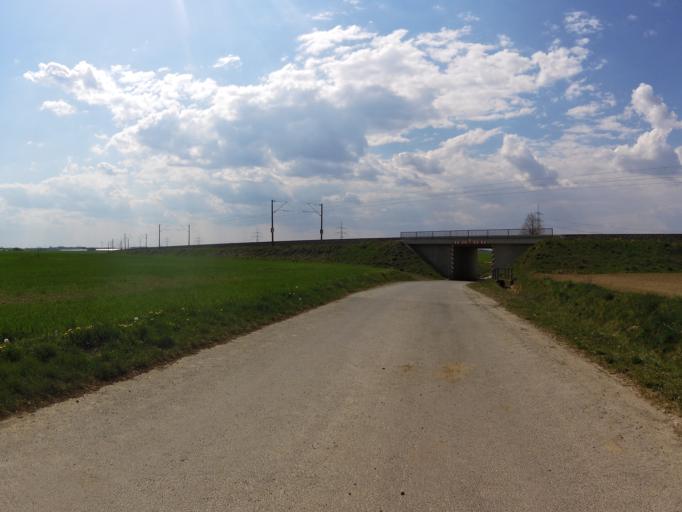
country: DE
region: Bavaria
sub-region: Regierungsbezirk Unterfranken
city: Oberpleichfeld
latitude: 49.8445
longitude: 10.1031
